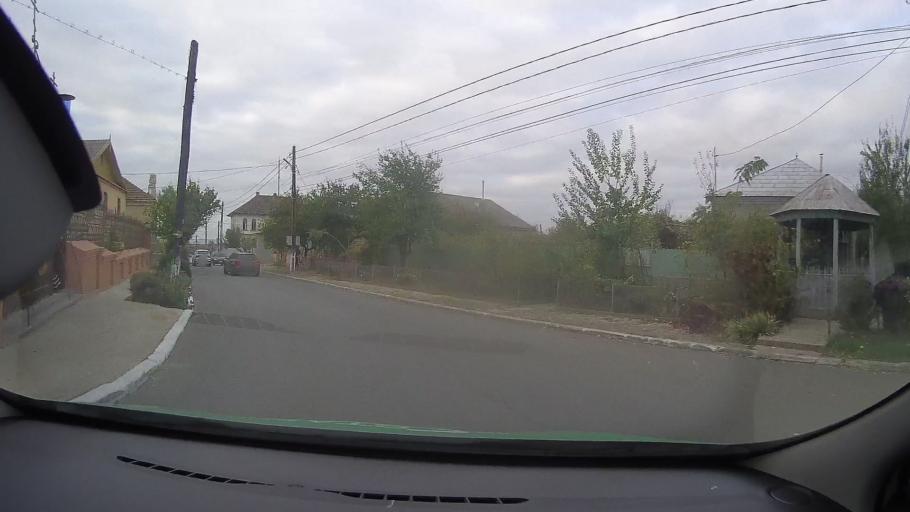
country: RO
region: Tulcea
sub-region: Comuna Jurilovca
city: Jurilovca
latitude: 44.7564
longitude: 28.8758
